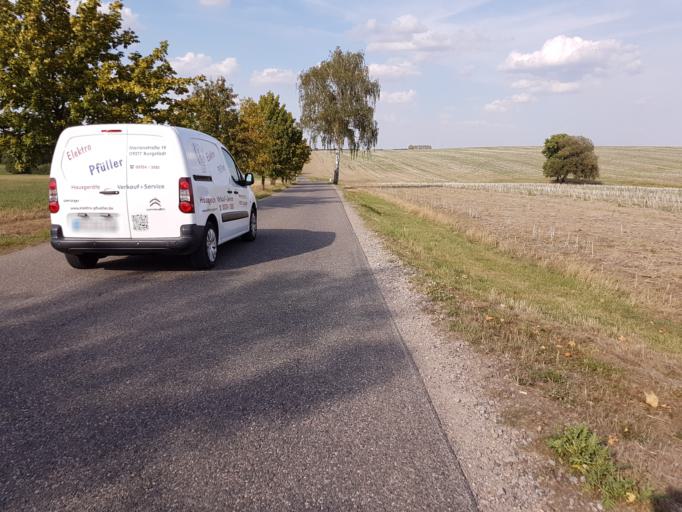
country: DE
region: Saxony
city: Claussnitz
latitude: 50.9577
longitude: 12.8816
